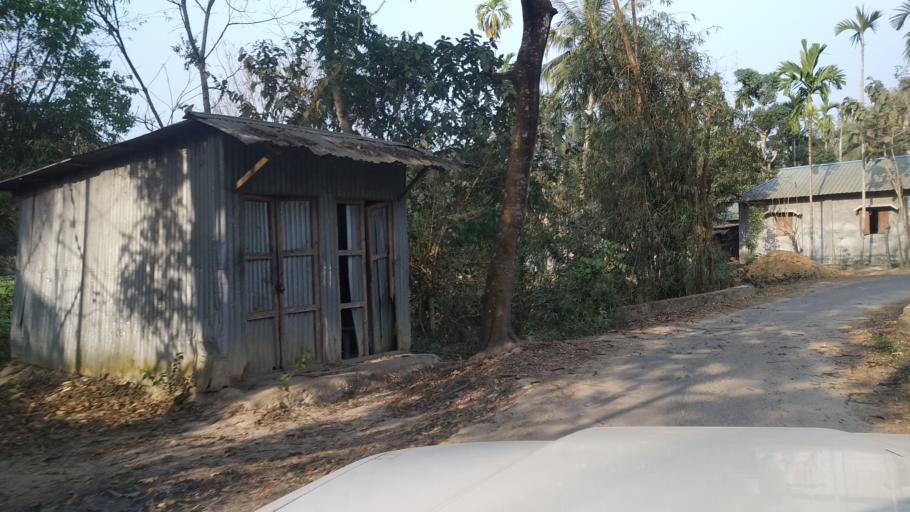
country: IN
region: Tripura
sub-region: West Tripura
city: Sonamura
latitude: 23.4301
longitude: 91.3069
